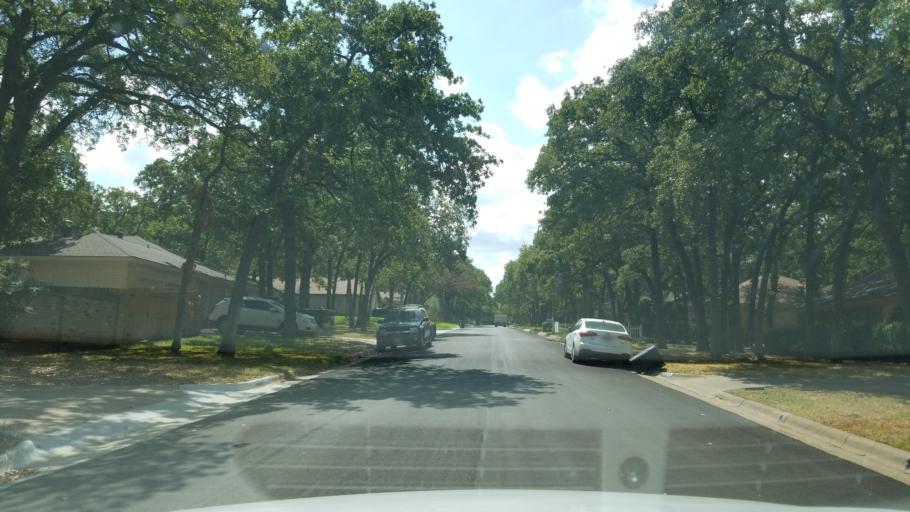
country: US
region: Texas
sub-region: Tarrant County
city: Euless
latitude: 32.8589
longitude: -97.0863
